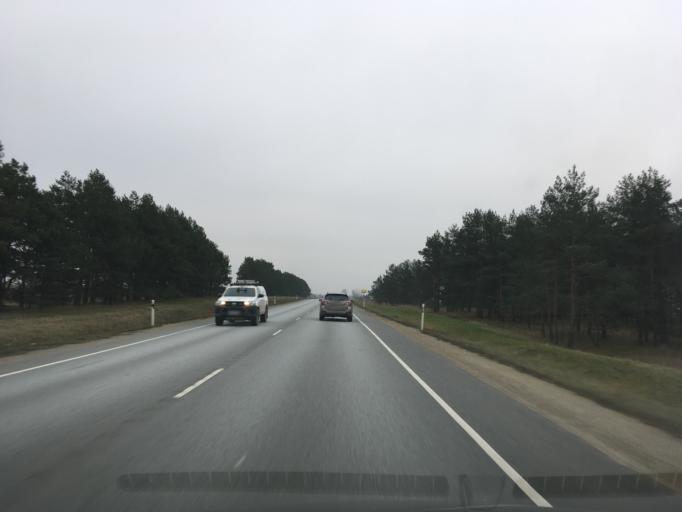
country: EE
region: Ida-Virumaa
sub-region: Puessi linn
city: Pussi
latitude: 59.4063
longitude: 27.0596
